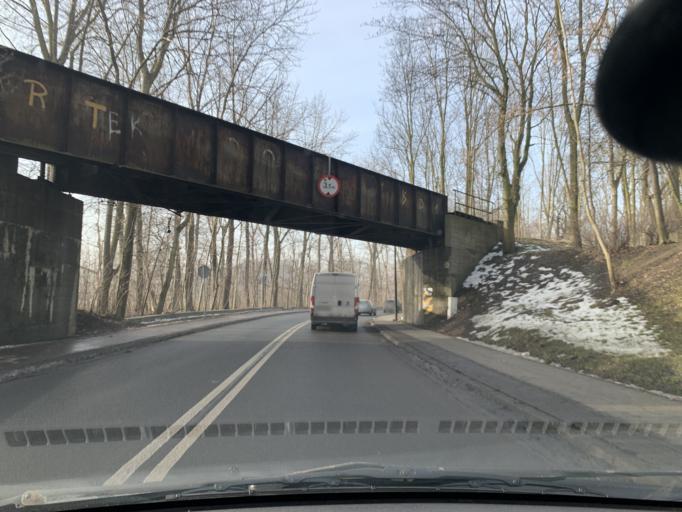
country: PL
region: Silesian Voivodeship
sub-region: Swietochlowice
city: Swietochlowice
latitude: 50.3264
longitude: 18.8603
